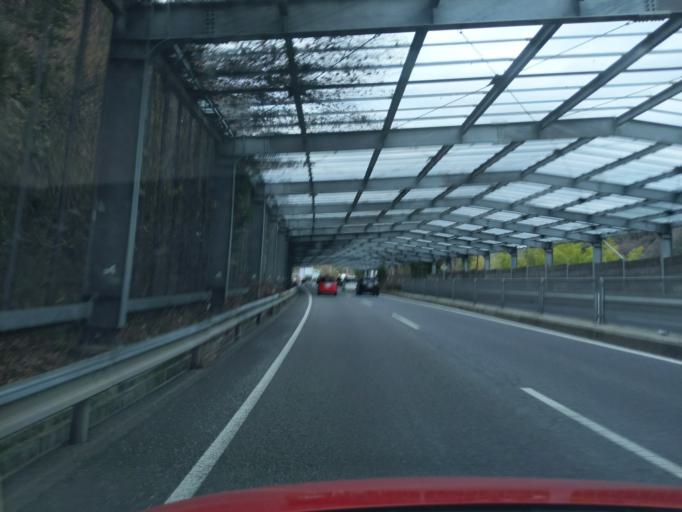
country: JP
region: Gifu
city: Tajimi
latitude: 35.3216
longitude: 137.0533
